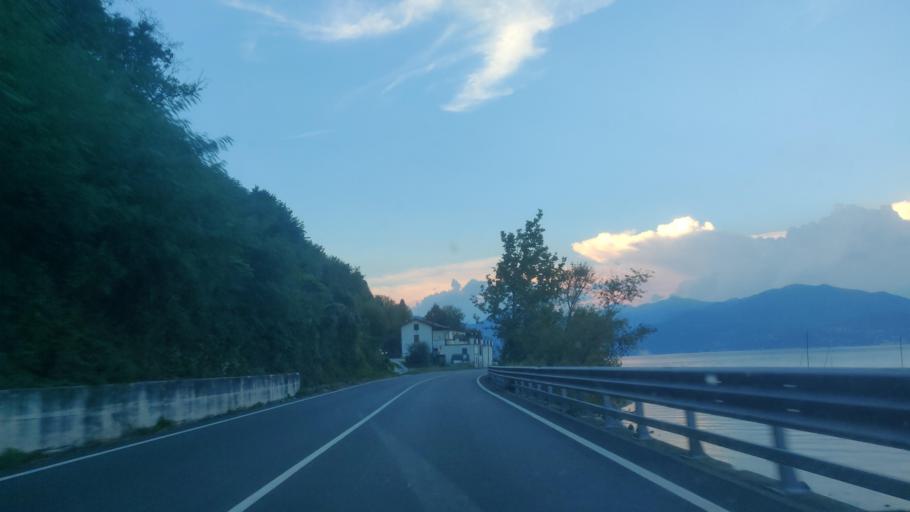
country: IT
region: Piedmont
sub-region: Provincia Verbano-Cusio-Ossola
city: Oggebbio
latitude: 45.9756
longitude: 8.6324
